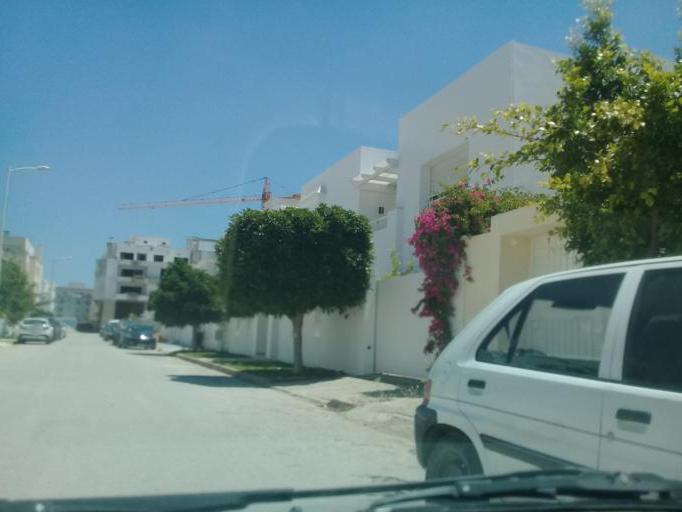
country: TN
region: Tunis
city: La Goulette
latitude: 36.8431
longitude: 10.2743
